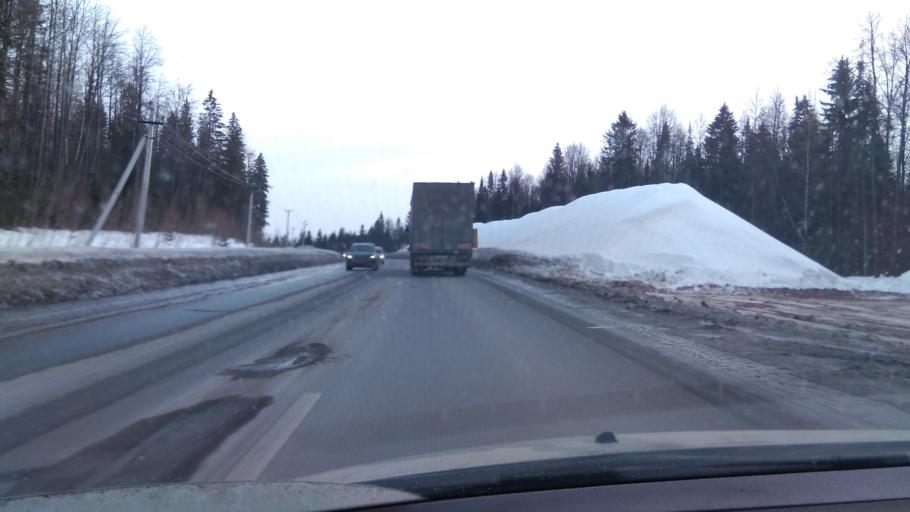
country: RU
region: Perm
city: Ferma
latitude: 57.9897
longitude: 56.3819
